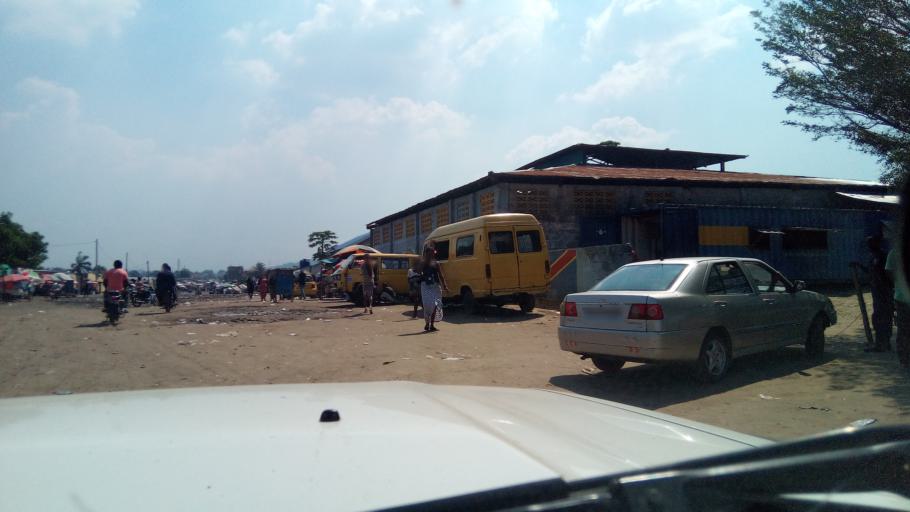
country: CD
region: Kinshasa
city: Kinshasa
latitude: -4.3604
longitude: 15.2981
